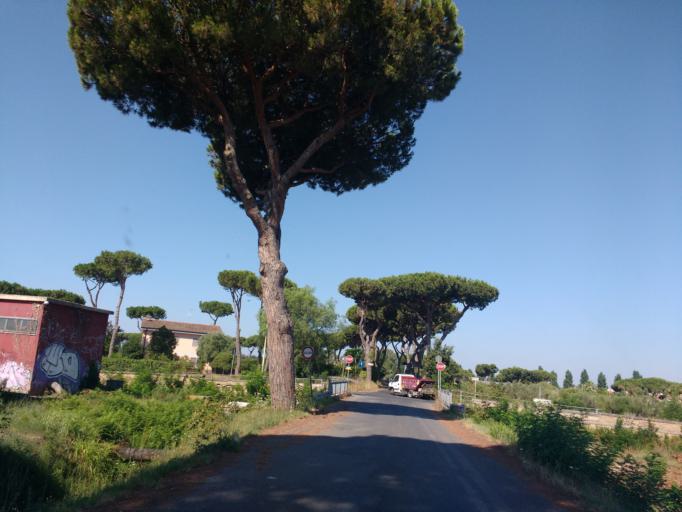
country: IT
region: Latium
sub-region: Citta metropolitana di Roma Capitale
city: Acilia-Castel Fusano-Ostia Antica
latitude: 41.7518
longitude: 12.3307
